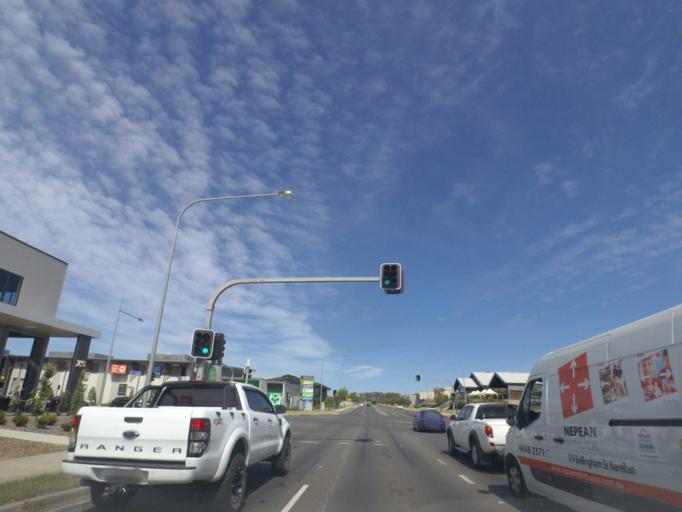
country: AU
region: New South Wales
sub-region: Camden
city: Narellan
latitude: -34.0217
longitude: 150.7649
